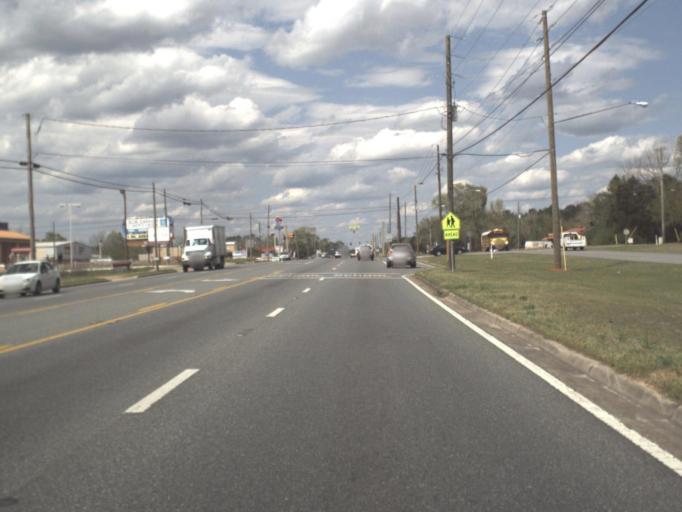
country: US
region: Florida
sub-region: Okaloosa County
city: Crestview
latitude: 30.7838
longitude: -86.5600
